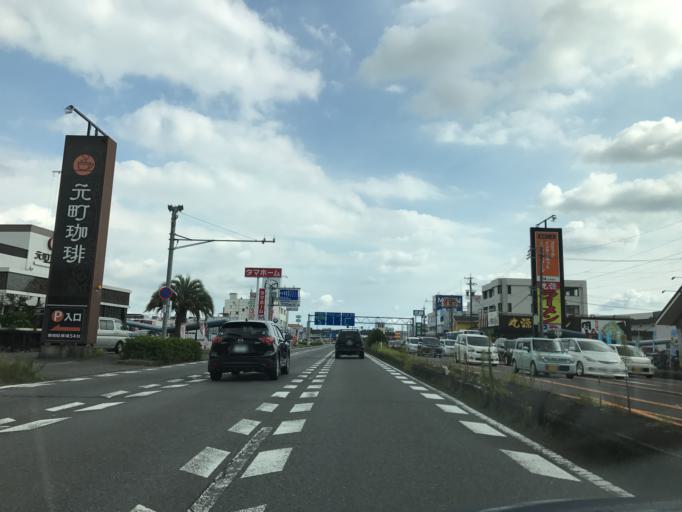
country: JP
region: Gifu
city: Kasamatsucho
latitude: 35.3932
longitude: 136.7852
